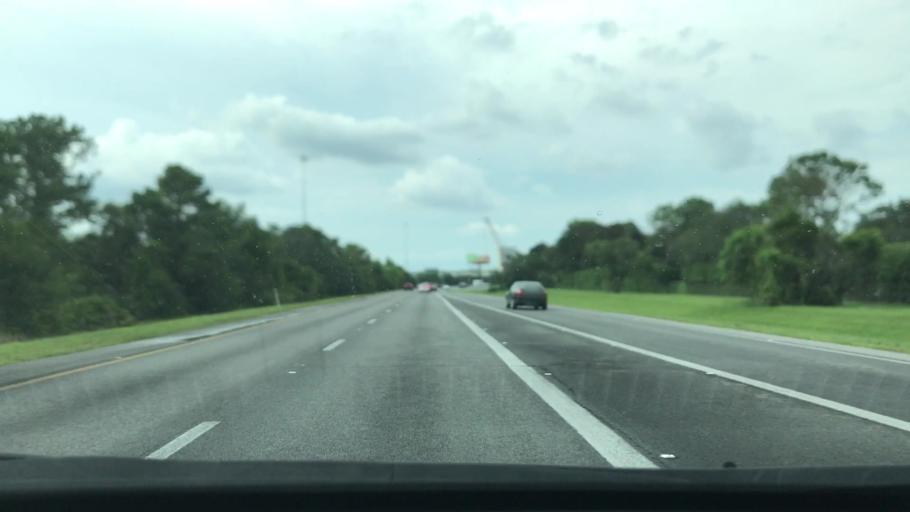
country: US
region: Florida
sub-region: Osceola County
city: Celebration
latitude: 28.3615
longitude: -81.5159
